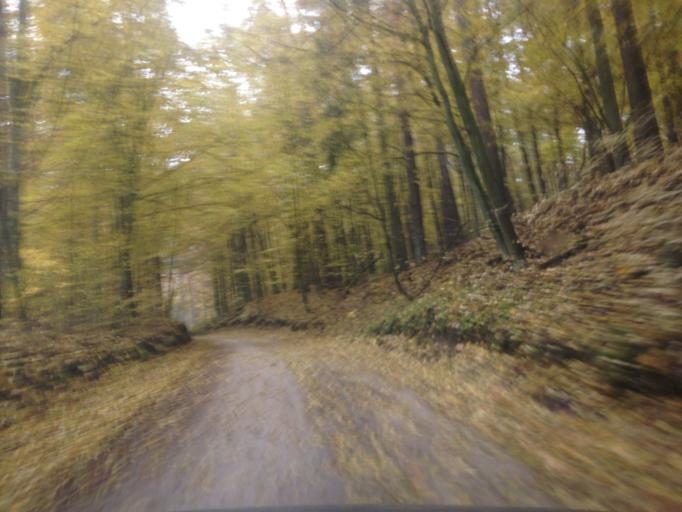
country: PL
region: Kujawsko-Pomorskie
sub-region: Powiat brodnicki
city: Gorzno
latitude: 53.2304
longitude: 19.7007
